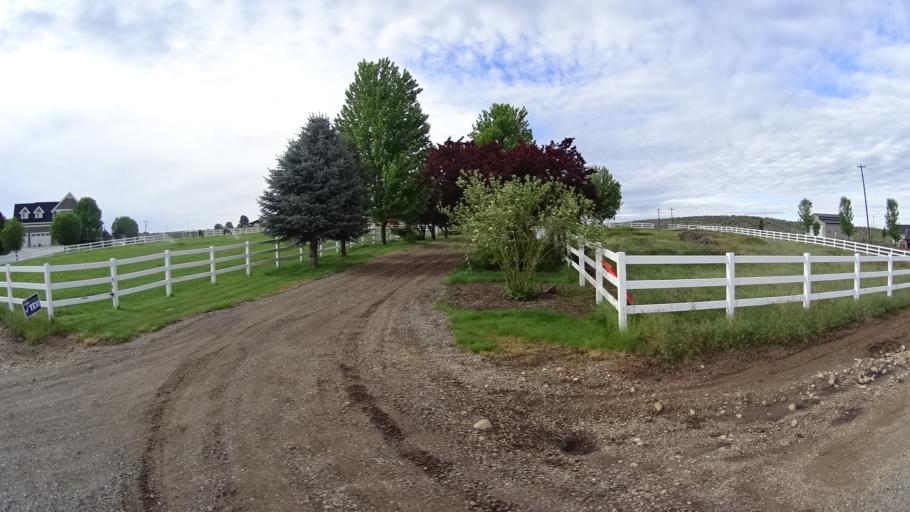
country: US
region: Idaho
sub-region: Ada County
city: Star
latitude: 43.7372
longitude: -116.5170
